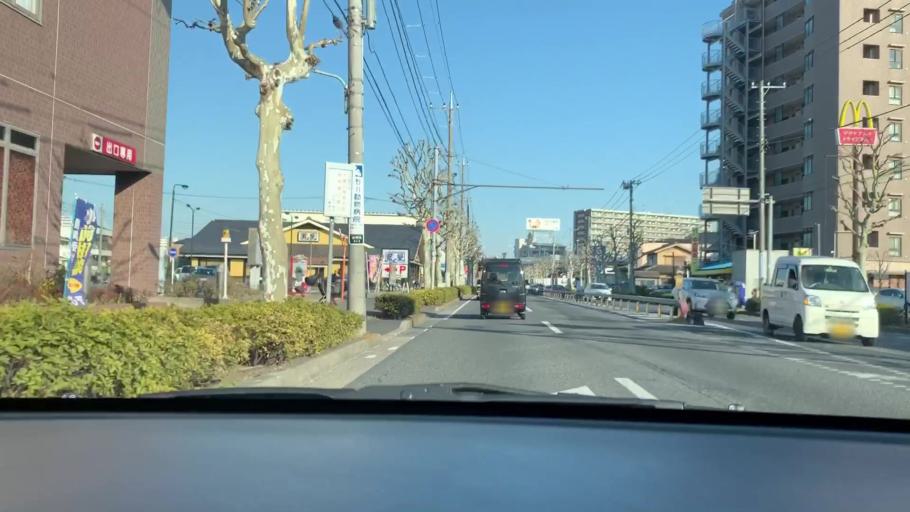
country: JP
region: Tokyo
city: Urayasu
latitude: 35.7019
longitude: 139.8935
